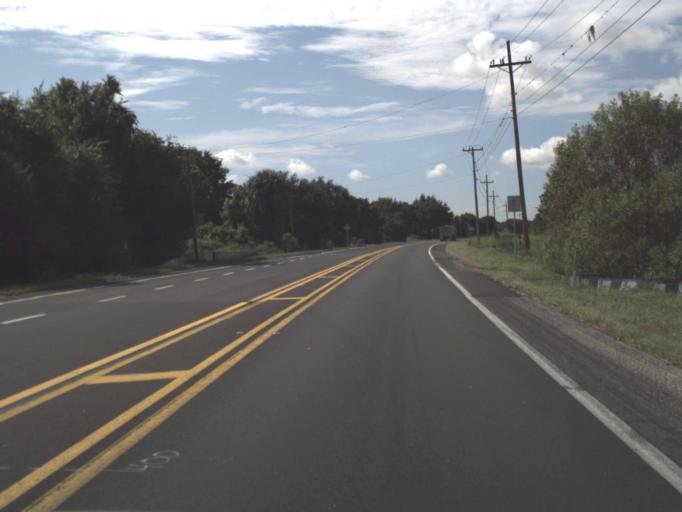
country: US
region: Florida
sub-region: Polk County
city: Combee Settlement
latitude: 28.1160
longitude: -81.9071
